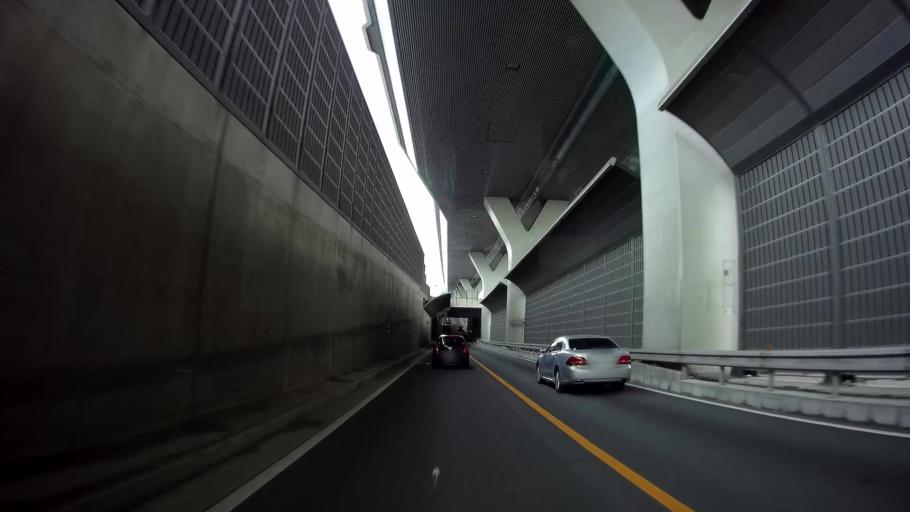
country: JP
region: Saitama
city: Yono
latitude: 35.8451
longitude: 139.6265
